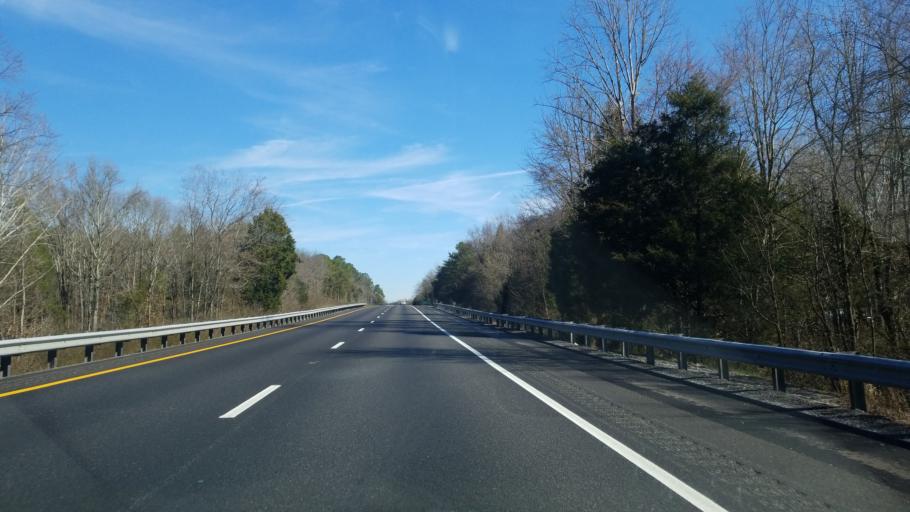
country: US
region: Tennessee
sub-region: McMinn County
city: Athens
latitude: 35.4014
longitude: -84.7094
